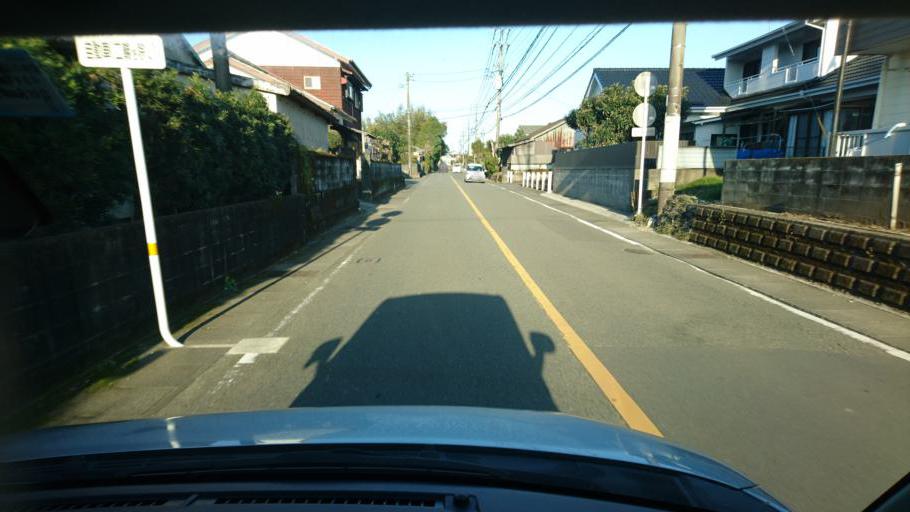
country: JP
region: Miyazaki
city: Miyazaki-shi
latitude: 31.8413
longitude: 131.4180
